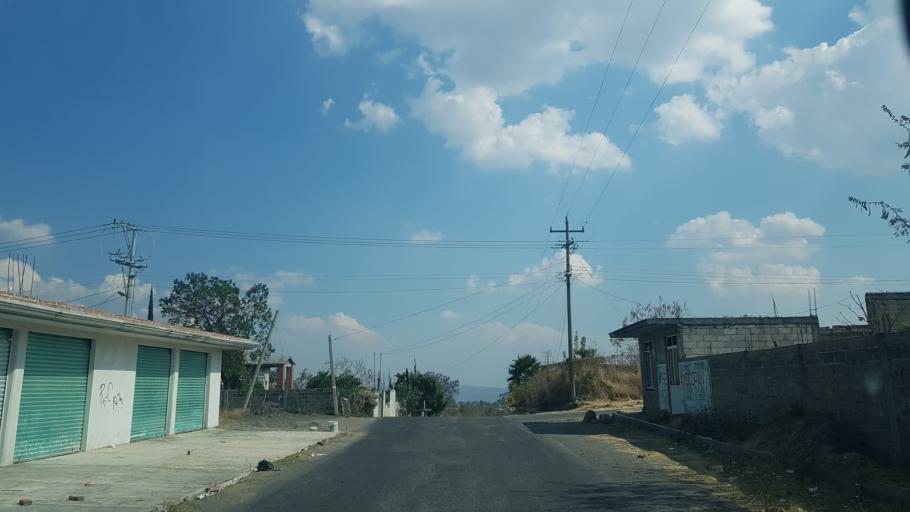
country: MX
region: Puebla
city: Atlixco
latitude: 18.9162
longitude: -98.4797
